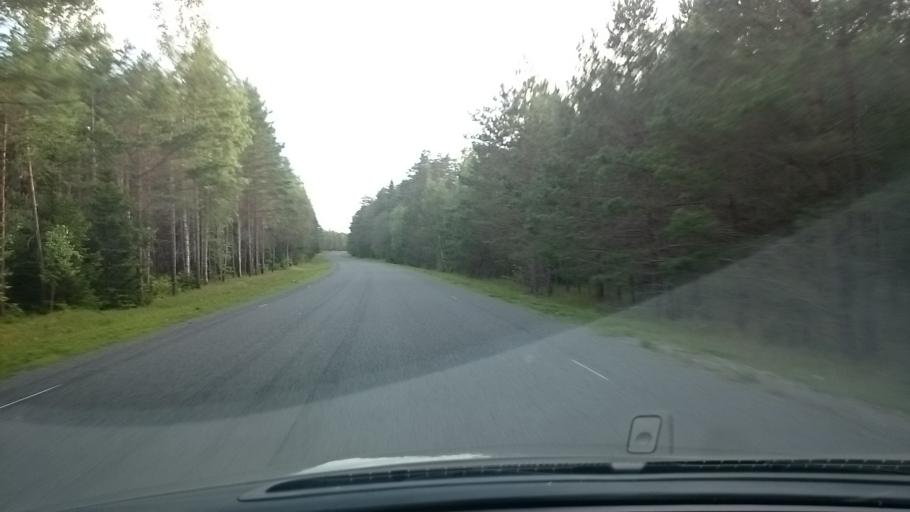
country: EE
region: Saare
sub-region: Kuressaare linn
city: Kuressaare
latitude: 58.4361
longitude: 22.2168
